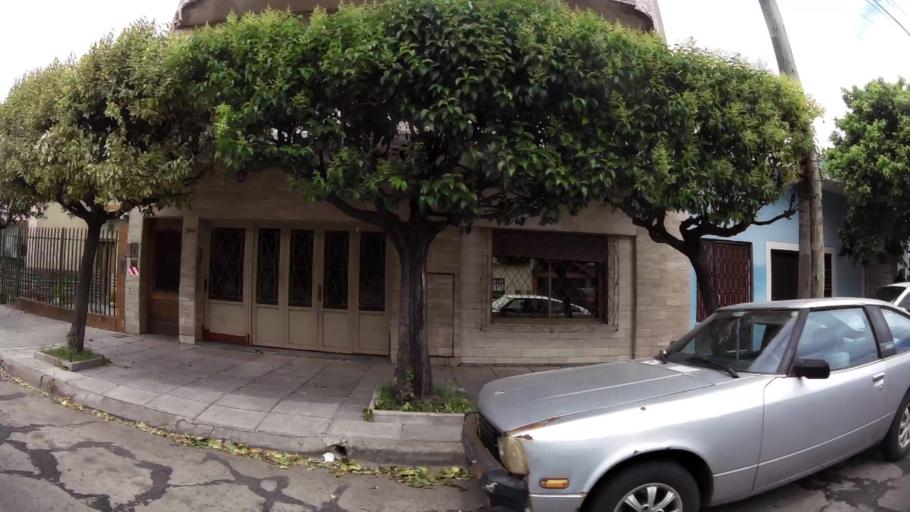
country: AR
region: Buenos Aires
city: San Justo
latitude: -34.6755
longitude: -58.5416
